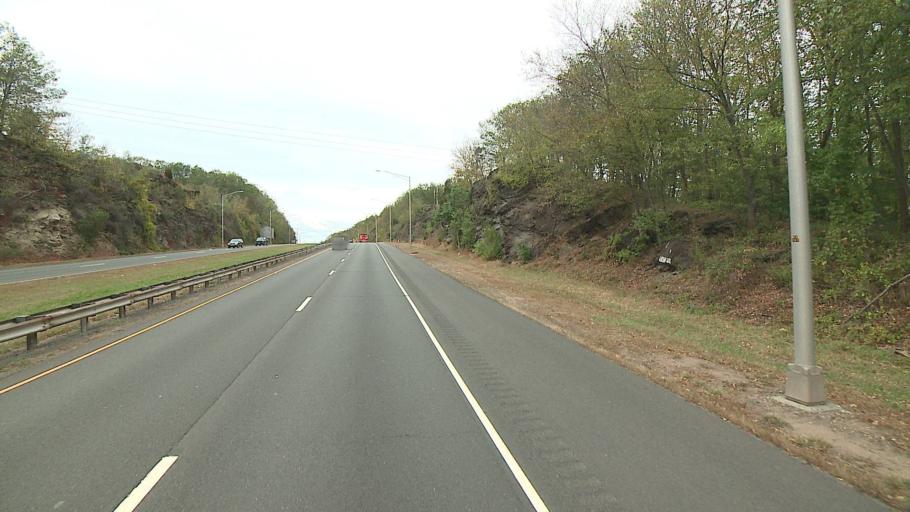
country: US
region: Connecticut
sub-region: Middlesex County
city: Higganum
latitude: 41.5212
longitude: -72.6055
